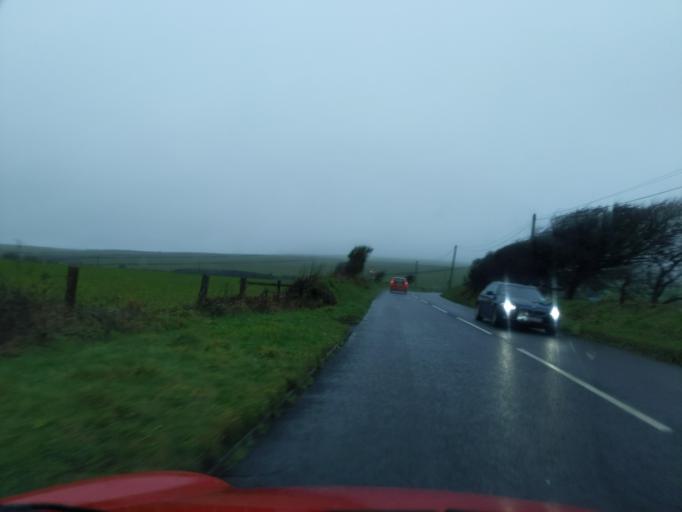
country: GB
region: England
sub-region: Cornwall
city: Camelford
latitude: 50.6449
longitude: -4.6970
